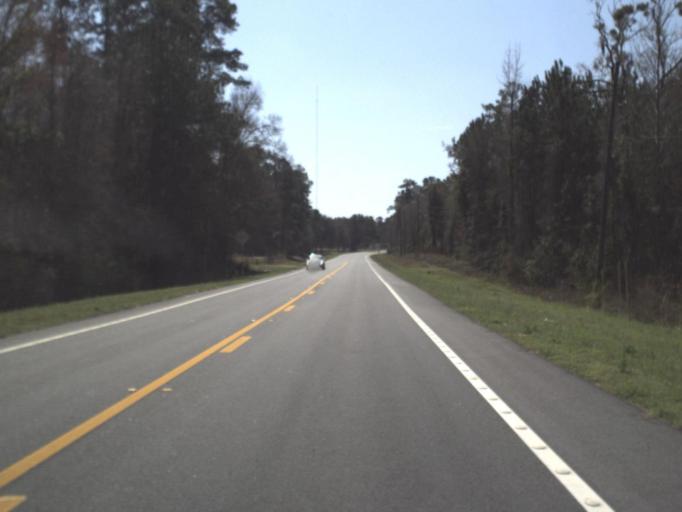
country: US
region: Florida
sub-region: Jefferson County
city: Monticello
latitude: 30.4733
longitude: -84.0215
